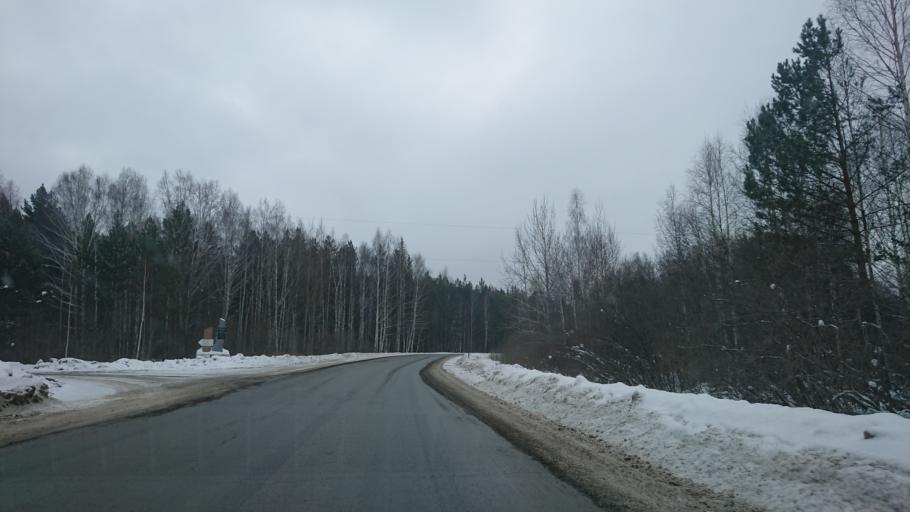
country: RU
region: Sverdlovsk
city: Sysert'
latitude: 56.4446
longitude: 60.8829
